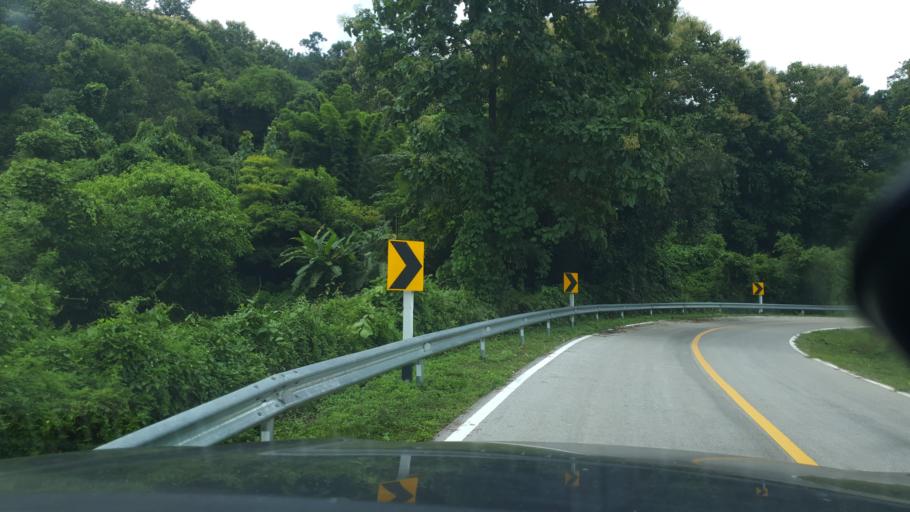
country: TH
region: Lamphun
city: Mae Tha
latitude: 18.4457
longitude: 99.2673
